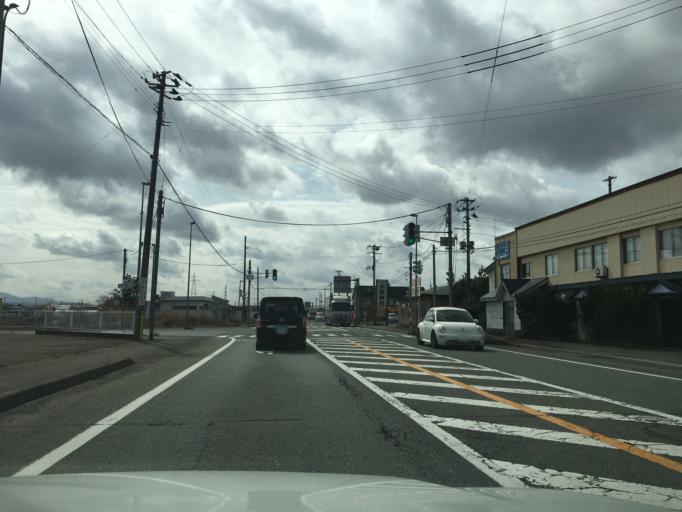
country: JP
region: Akita
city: Tenno
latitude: 39.9497
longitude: 140.0833
